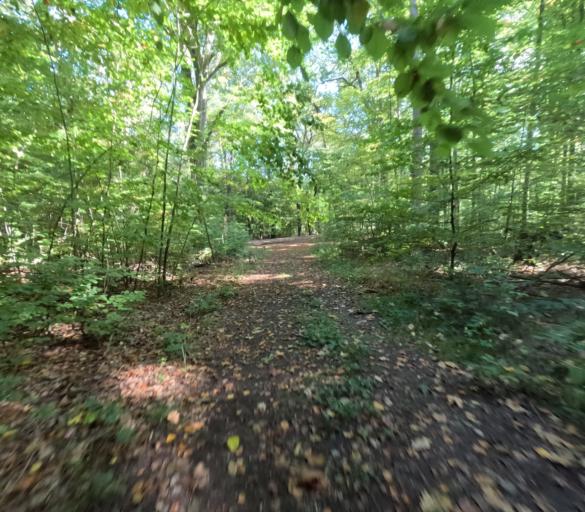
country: DE
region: Saxony
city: Moritzburg
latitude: 51.1676
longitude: 13.6672
